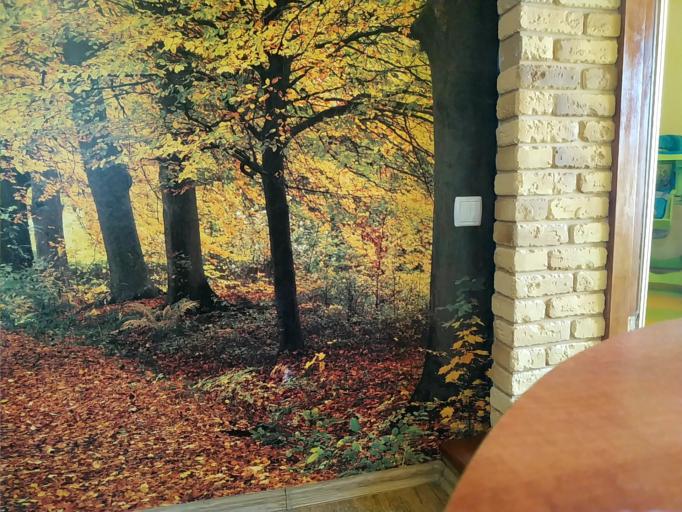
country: RU
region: Arkhangelskaya
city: Onega
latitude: 63.7413
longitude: 38.0796
